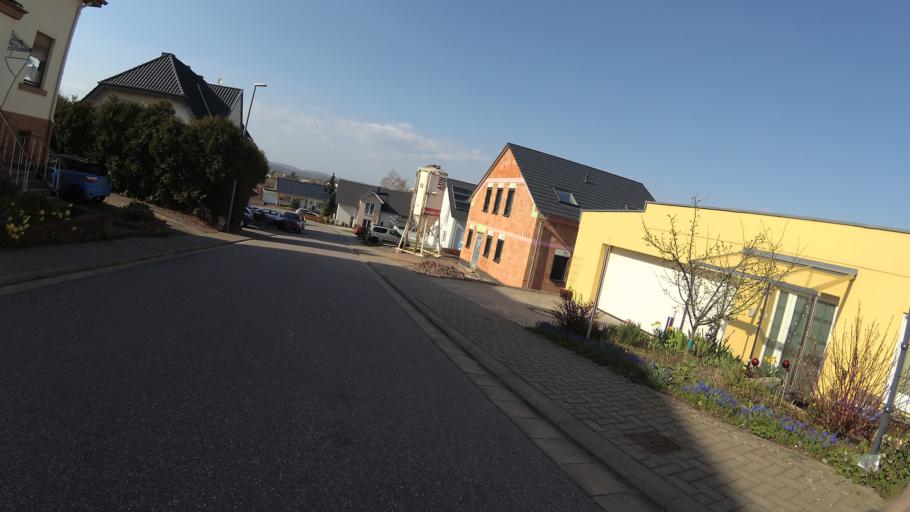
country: DE
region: Saarland
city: Heusweiler
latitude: 49.3311
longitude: 6.9460
